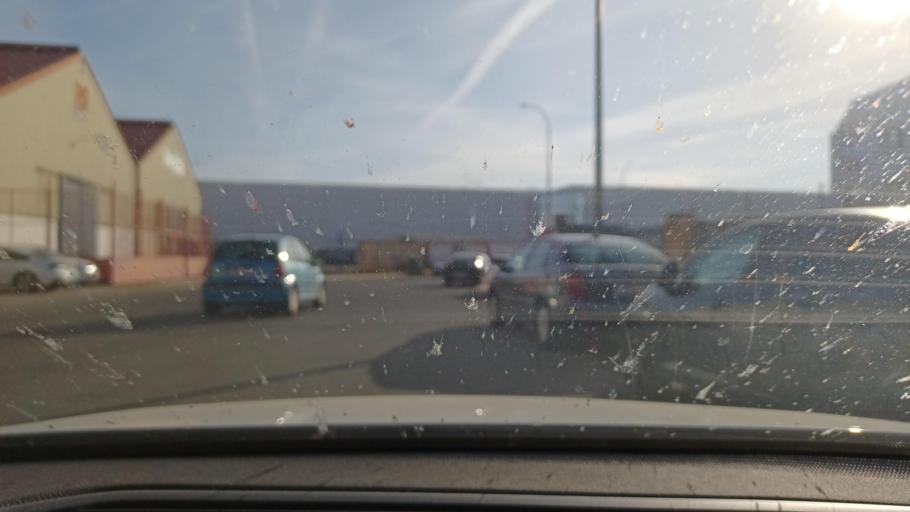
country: ES
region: Castille-La Mancha
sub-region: Provincia de Guadalajara
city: Alovera
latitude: 40.5946
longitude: -3.2350
